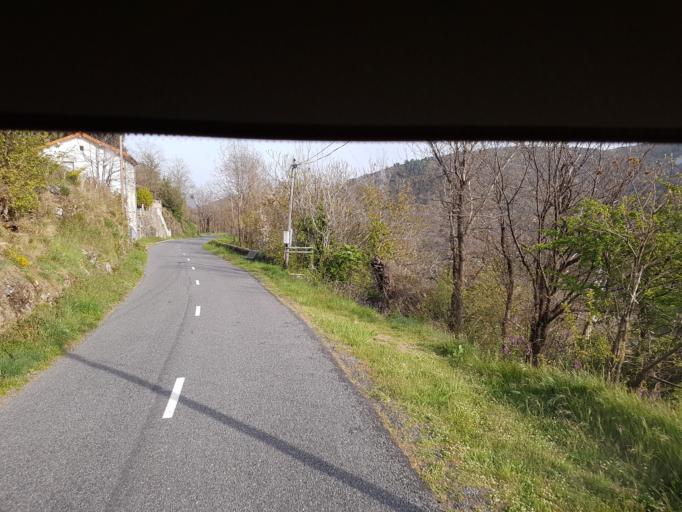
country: FR
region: Languedoc-Roussillon
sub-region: Departement du Gard
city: Branoux-les-Taillades
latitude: 44.3315
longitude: 3.8855
